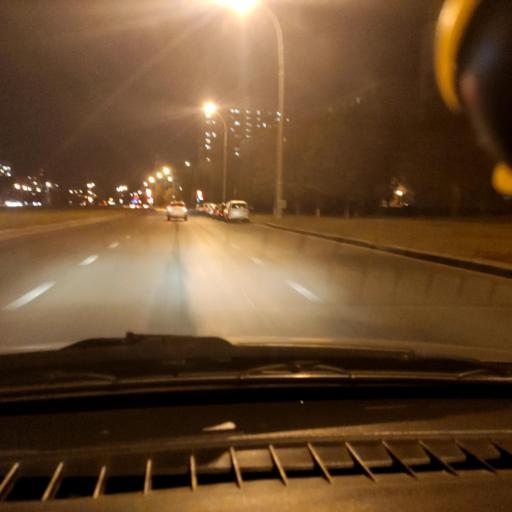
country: RU
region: Samara
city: Tol'yatti
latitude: 53.5286
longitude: 49.2869
